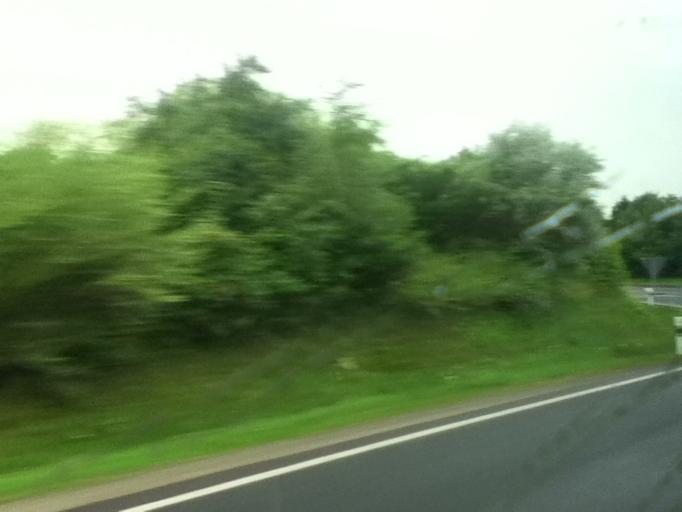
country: DE
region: Thuringia
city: Kirchheim
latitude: 50.9045
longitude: 11.0082
